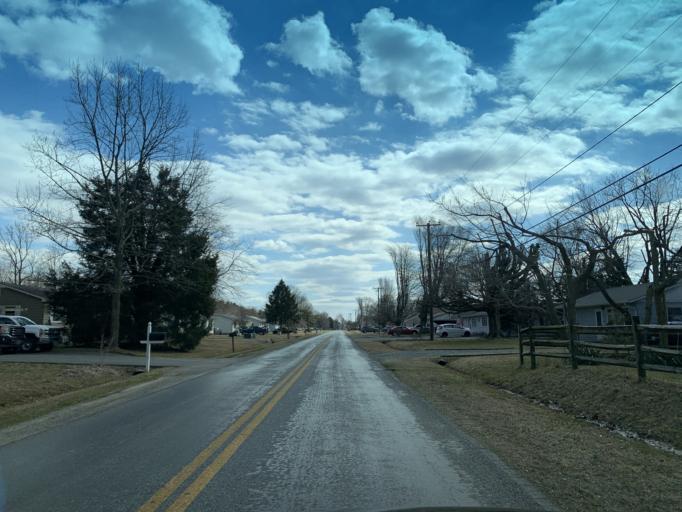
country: US
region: Maryland
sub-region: Queen Anne's County
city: Chester
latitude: 38.9395
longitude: -76.2662
